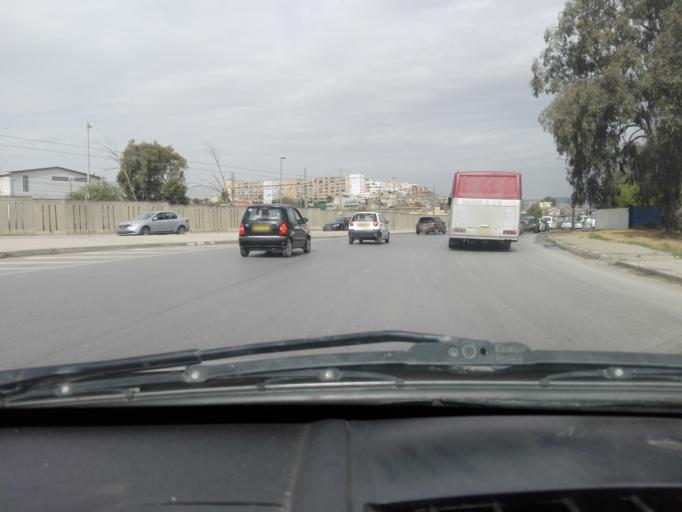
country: DZ
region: Alger
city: Bab Ezzouar
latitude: 36.7311
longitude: 3.1274
